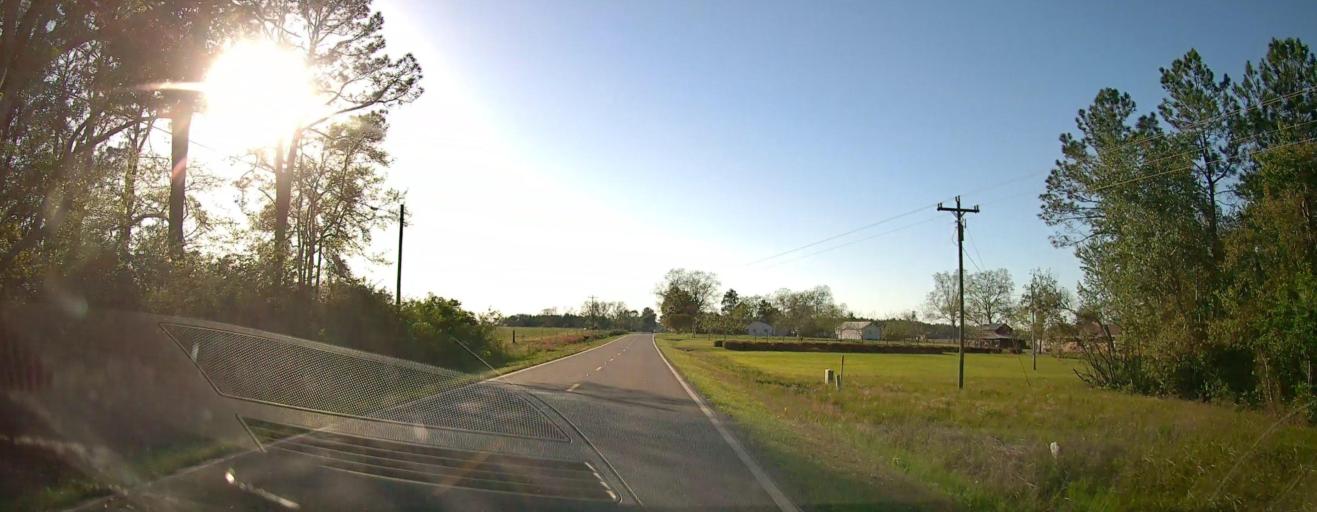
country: US
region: Georgia
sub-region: Ben Hill County
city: Fitzgerald
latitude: 31.6812
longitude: -83.2013
